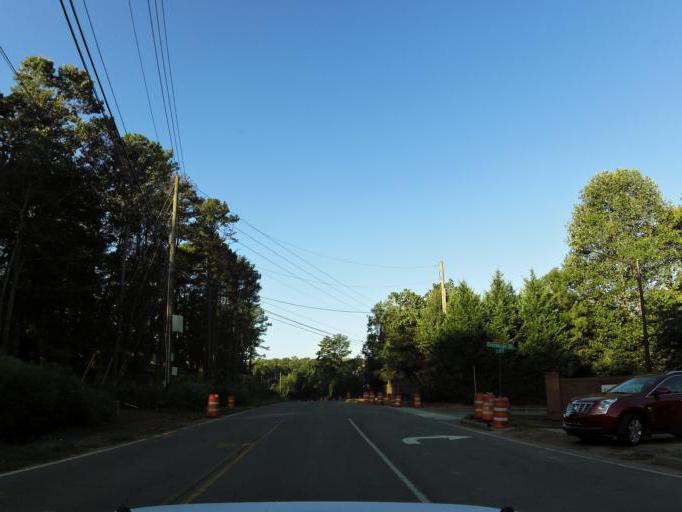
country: US
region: Georgia
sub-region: Cobb County
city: Kennesaw
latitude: 34.0057
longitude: -84.6367
